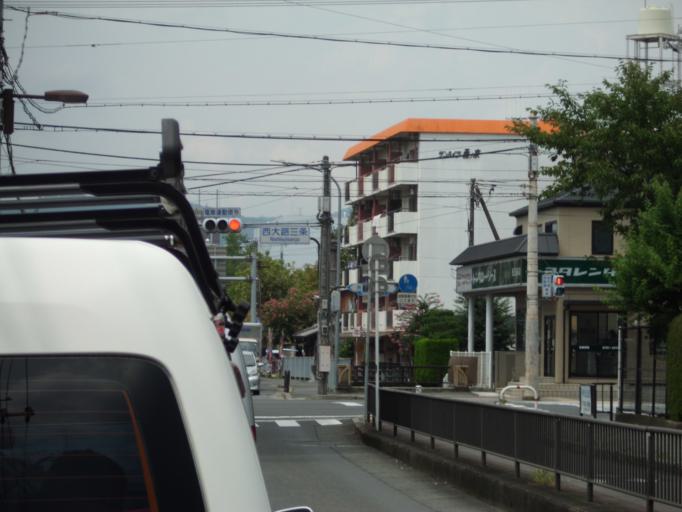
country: JP
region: Kyoto
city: Kyoto
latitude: 35.0084
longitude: 135.7361
